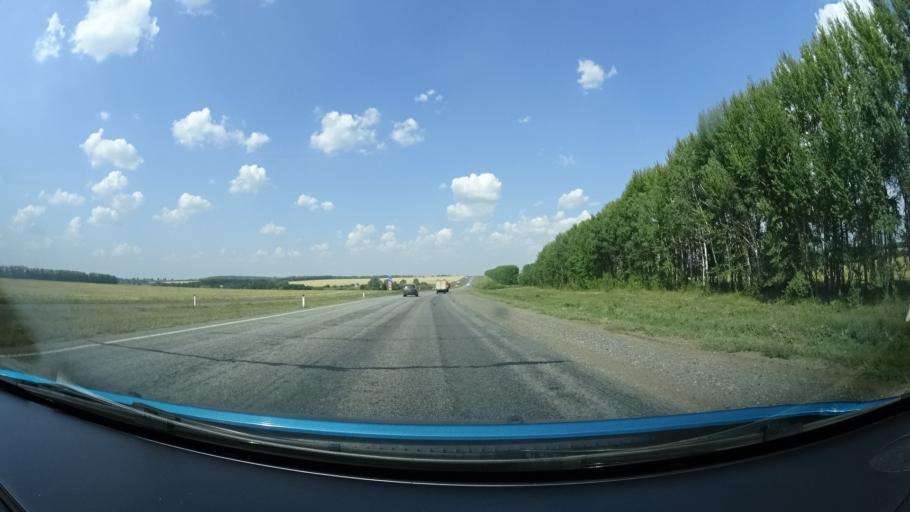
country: RU
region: Bashkortostan
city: Dmitriyevka
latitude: 54.6977
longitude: 55.2683
